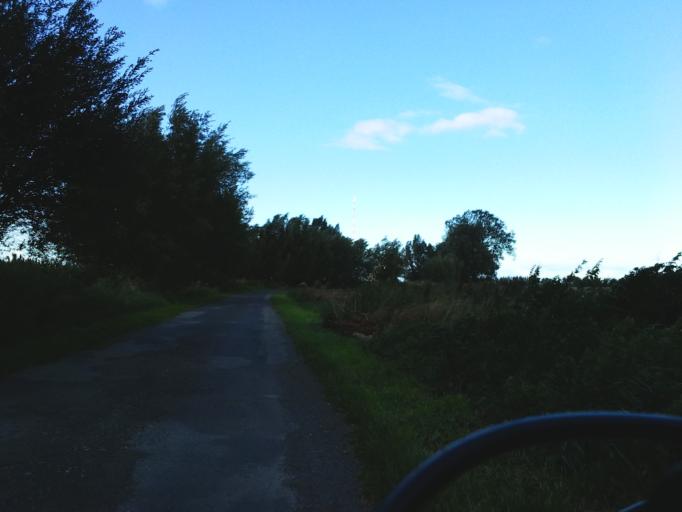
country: DE
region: Mecklenburg-Vorpommern
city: Dierkow-West
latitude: 54.1136
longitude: 12.1217
